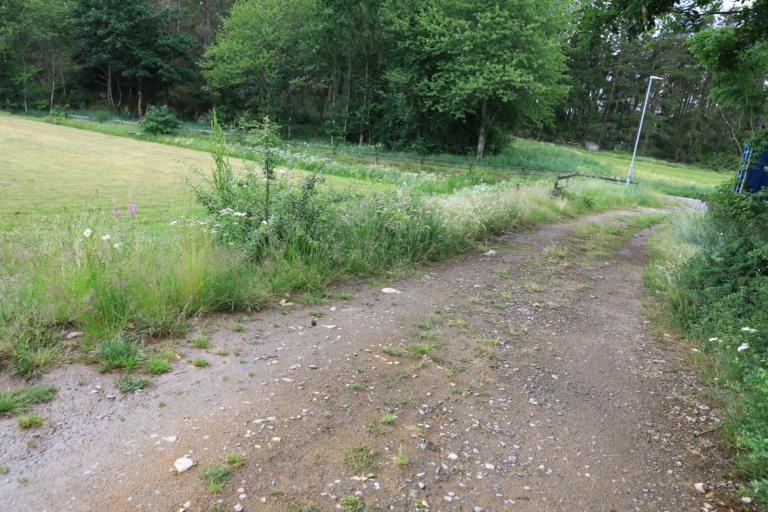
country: SE
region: Halland
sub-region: Varbergs Kommun
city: Varberg
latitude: 57.1709
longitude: 12.2878
